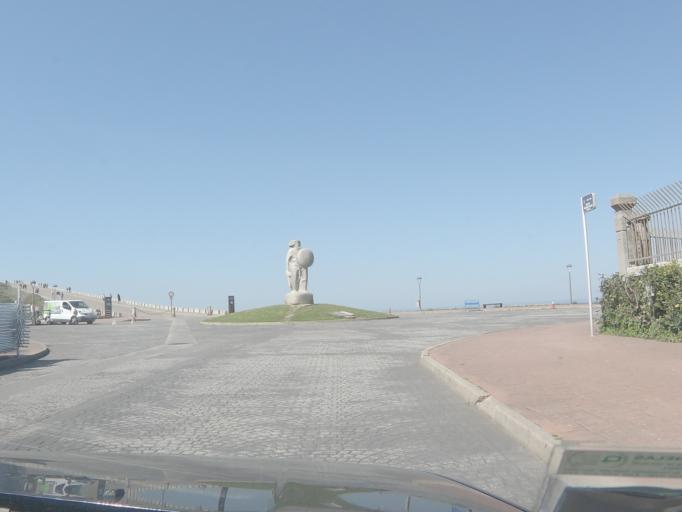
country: ES
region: Galicia
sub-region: Provincia da Coruna
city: A Coruna
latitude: 43.3845
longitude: -8.4023
